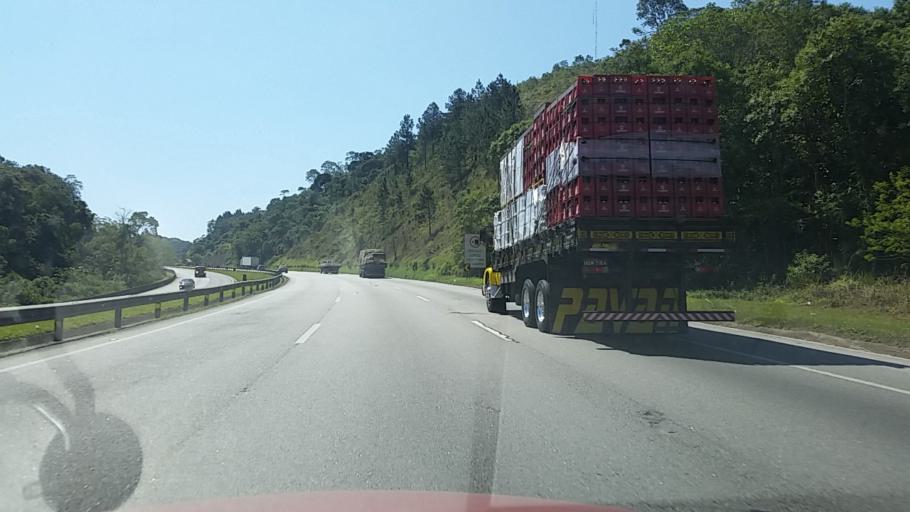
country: BR
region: Sao Paulo
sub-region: Juquitiba
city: Juquitiba
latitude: -23.9940
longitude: -47.1475
